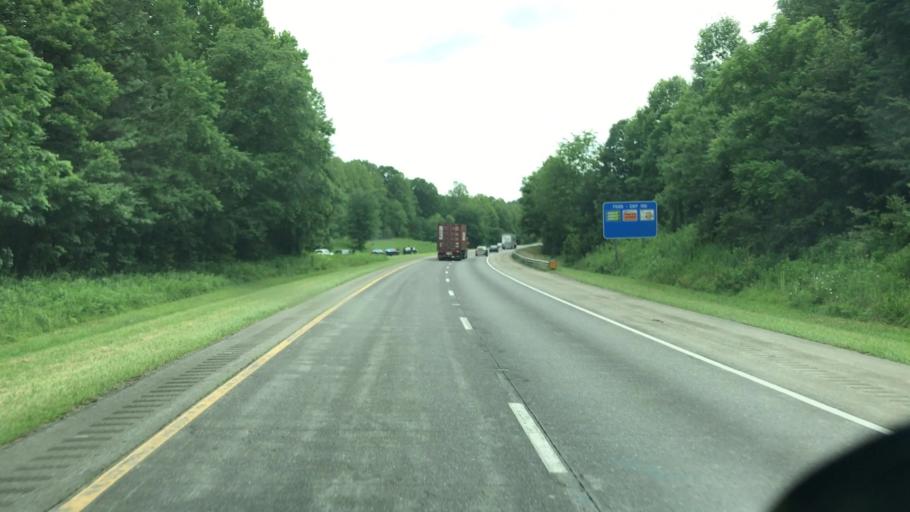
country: US
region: North Carolina
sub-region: Surry County
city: Dobson
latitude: 36.4942
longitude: -80.7437
